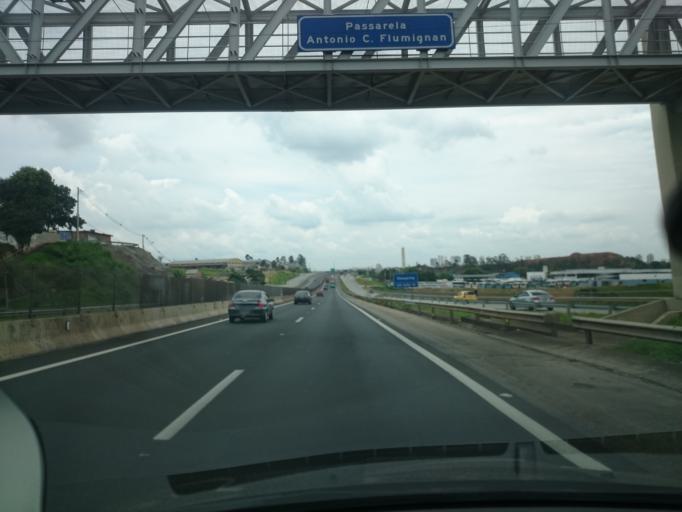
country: BR
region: Sao Paulo
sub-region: Votorantim
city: Votorantim
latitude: -23.5209
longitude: -47.4363
